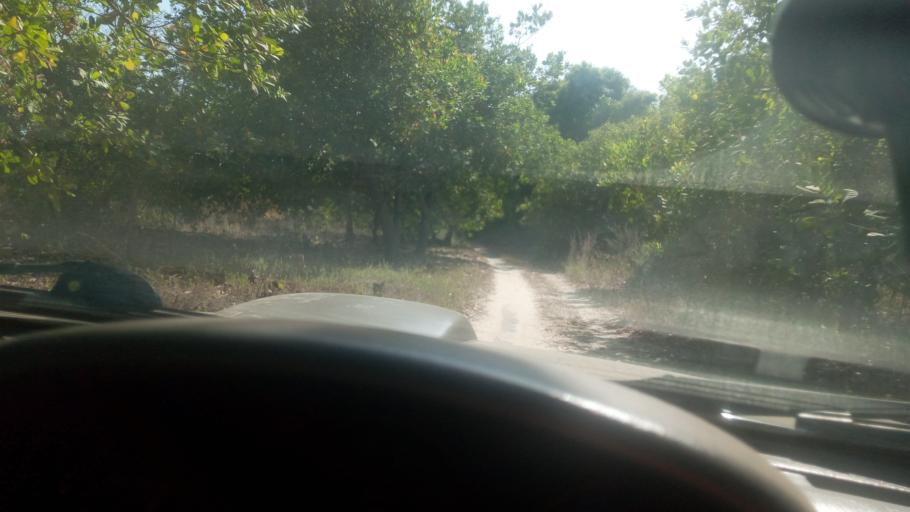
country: GW
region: Oio
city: Farim
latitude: 12.4463
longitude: -15.4339
